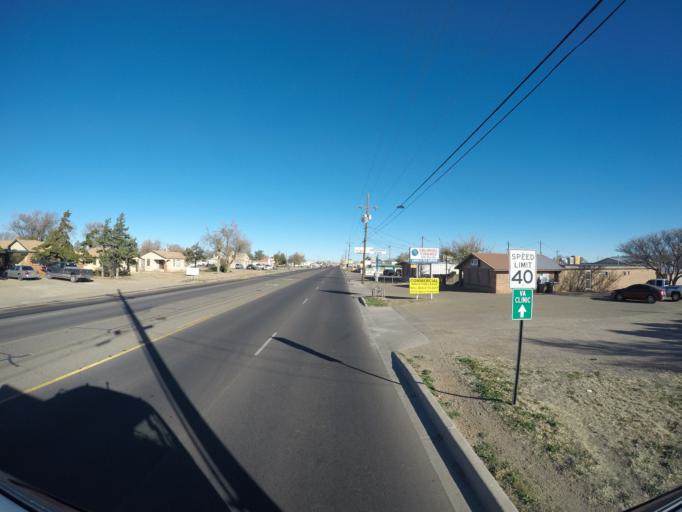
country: US
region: New Mexico
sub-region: Curry County
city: Clovis
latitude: 34.4273
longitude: -103.1964
